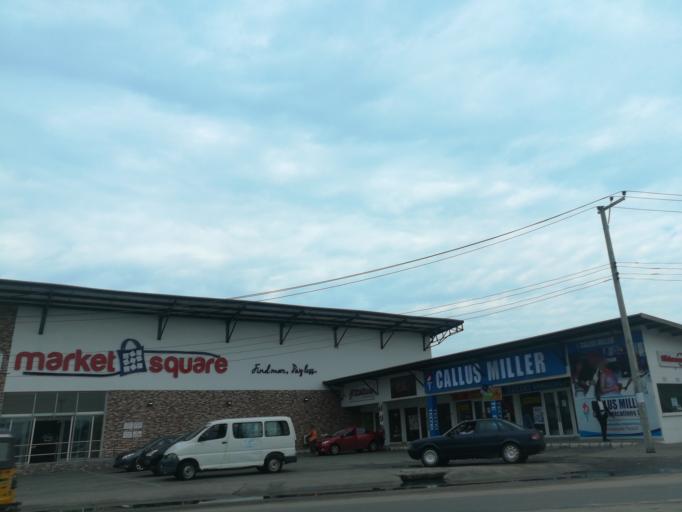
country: NG
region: Rivers
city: Port Harcourt
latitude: 4.8478
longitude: 6.9746
